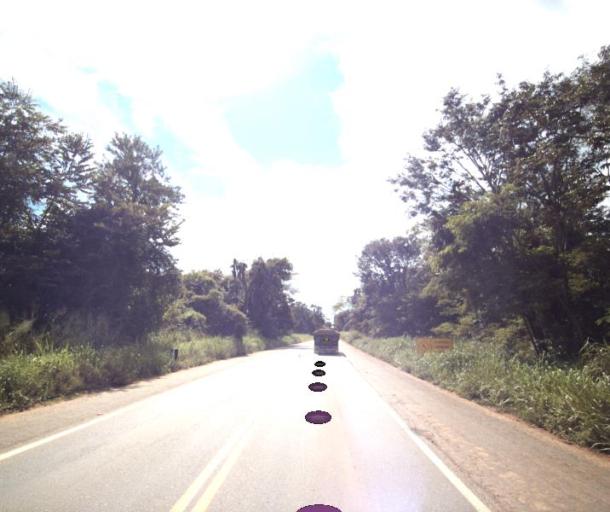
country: BR
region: Goias
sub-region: Petrolina De Goias
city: Petrolina de Goias
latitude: -15.9594
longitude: -49.1811
